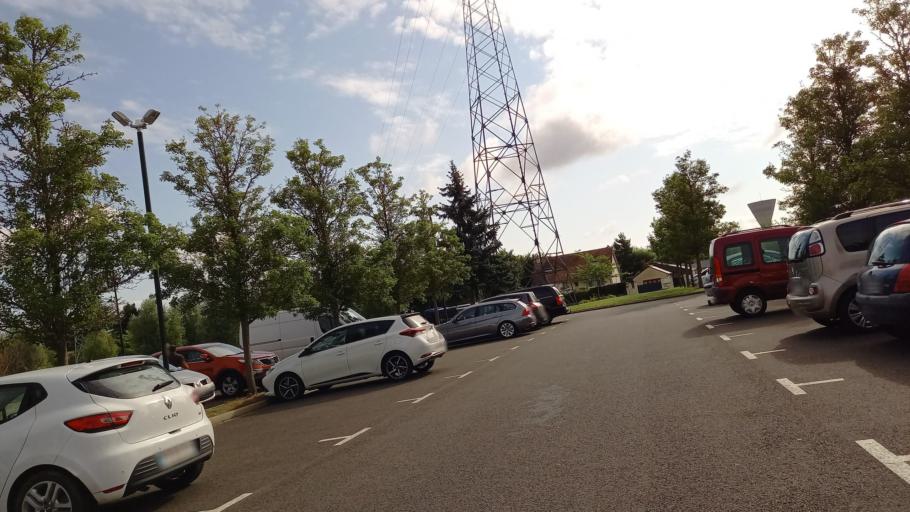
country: FR
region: Centre
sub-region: Departement d'Indre-et-Loire
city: Saint-Cyr-sur-Loire
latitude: 47.4200
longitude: 0.6543
